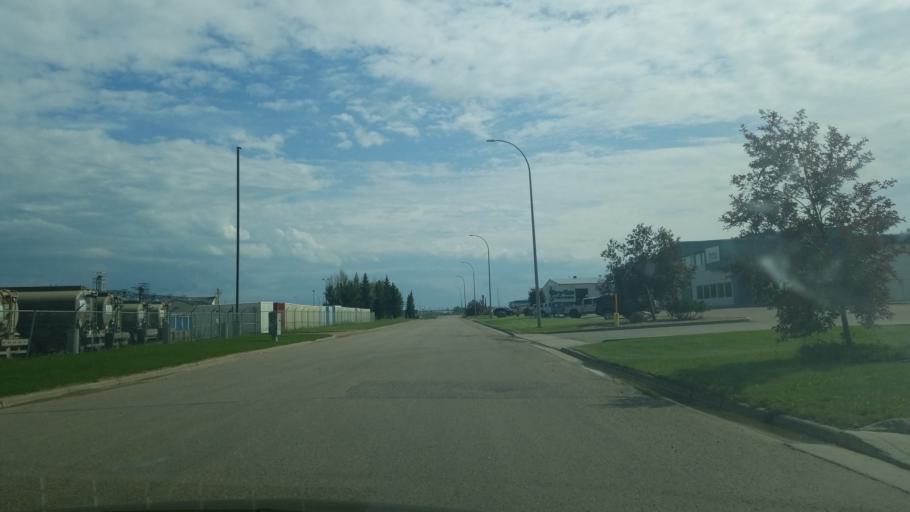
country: CA
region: Saskatchewan
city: Lloydminster
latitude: 53.2894
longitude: -110.0368
